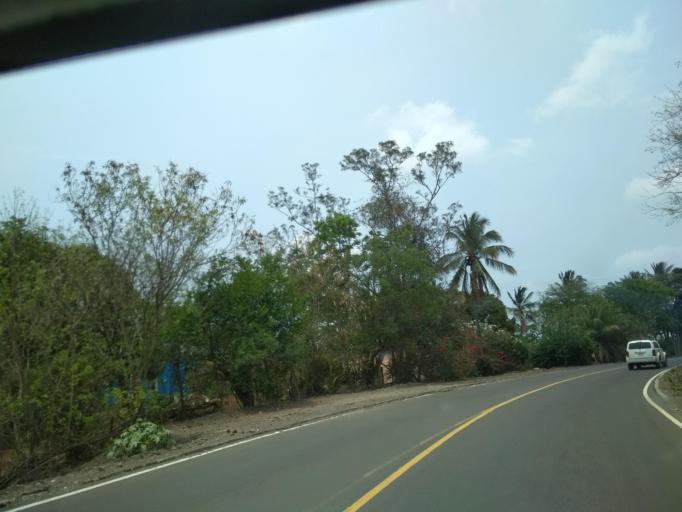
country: MX
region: Veracruz
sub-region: Veracruz
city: Delfino Victoria (Santa Fe)
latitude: 19.1683
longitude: -96.2866
